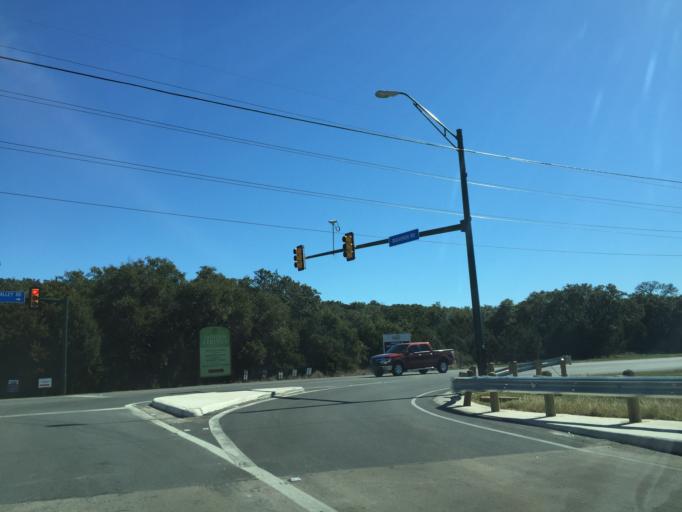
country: US
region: Texas
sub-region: Bexar County
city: Timberwood Park
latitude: 29.6871
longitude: -98.4428
